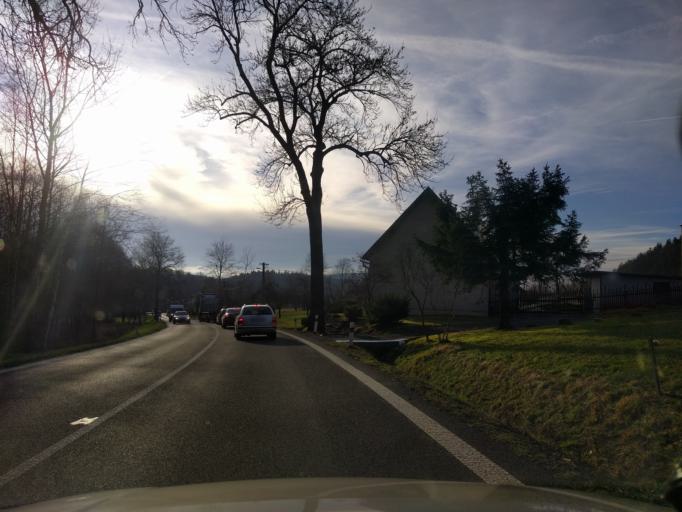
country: CZ
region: Liberecky
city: Mnisek
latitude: 50.8494
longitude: 15.0311
